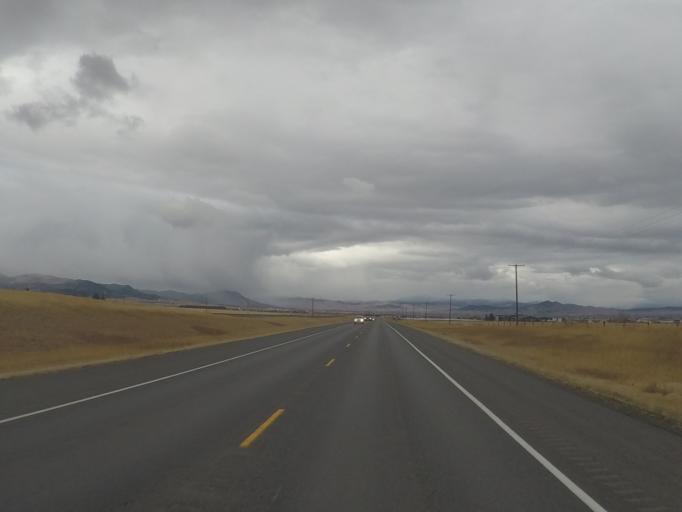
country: US
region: Montana
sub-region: Lewis and Clark County
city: East Helena
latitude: 46.5855
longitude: -111.8668
